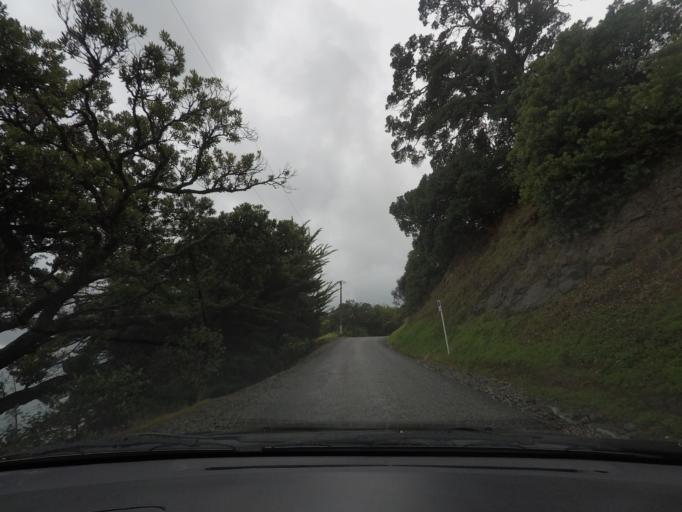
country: NZ
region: Auckland
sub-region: Auckland
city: Warkworth
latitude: -36.4852
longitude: 174.7242
